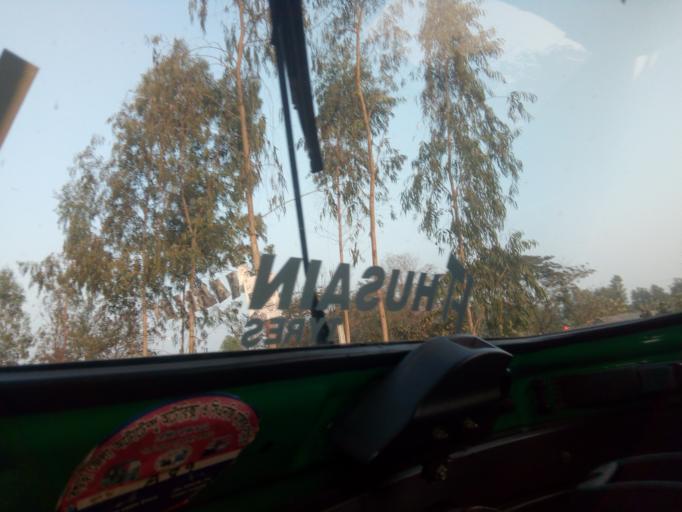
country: BD
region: Rajshahi
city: Bogra
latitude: 24.5559
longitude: 89.1969
